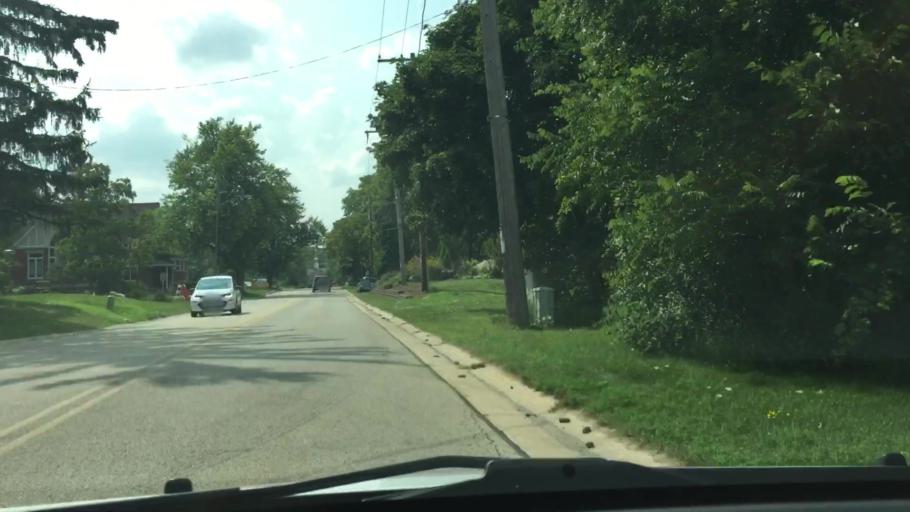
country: US
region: Wisconsin
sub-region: Waukesha County
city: Wales
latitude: 43.0057
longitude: -88.3791
